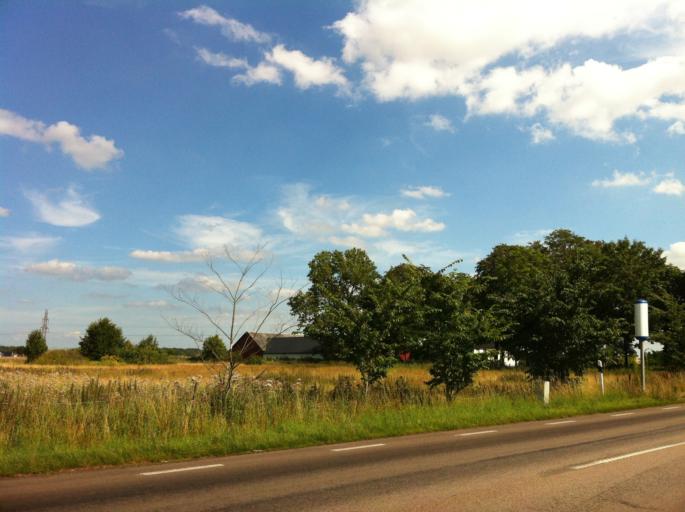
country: SE
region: Skane
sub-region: Helsingborg
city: Barslov
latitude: 55.9762
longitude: 12.8753
